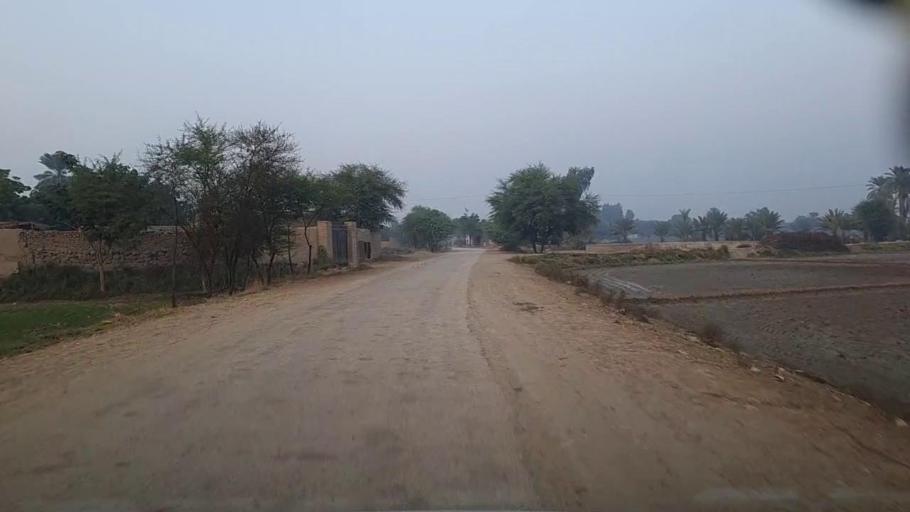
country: PK
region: Sindh
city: Bozdar
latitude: 27.0653
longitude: 68.5965
